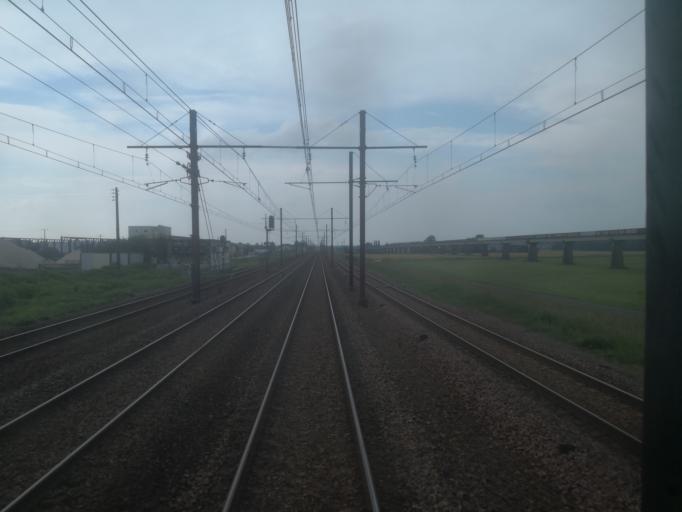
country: FR
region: Centre
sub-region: Departement du Loiret
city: Saran
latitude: 47.9765
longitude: 1.8865
